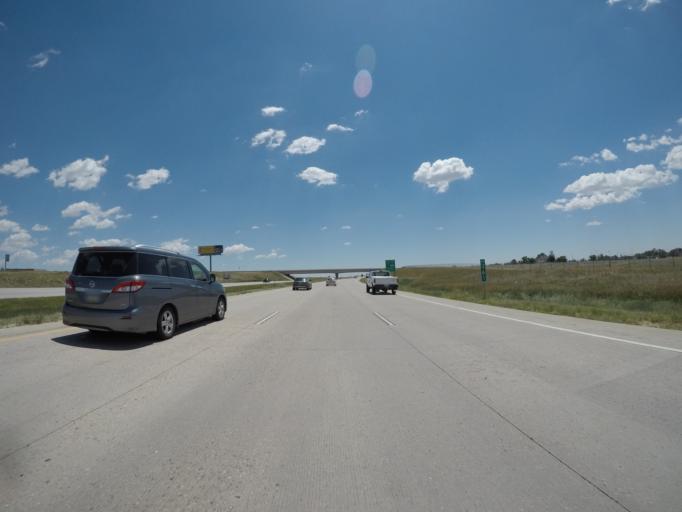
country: US
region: Colorado
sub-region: Lincoln County
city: Limon
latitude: 39.2717
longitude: -103.6801
